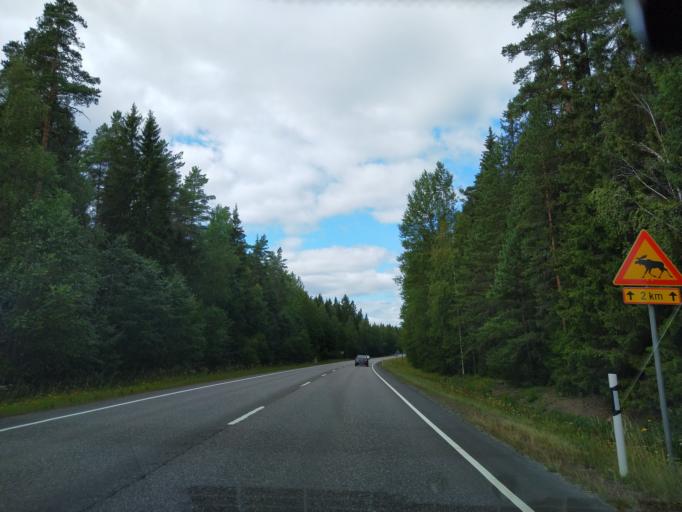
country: FI
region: Haeme
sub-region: Riihimaeki
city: Loppi
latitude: 60.7490
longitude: 24.3223
